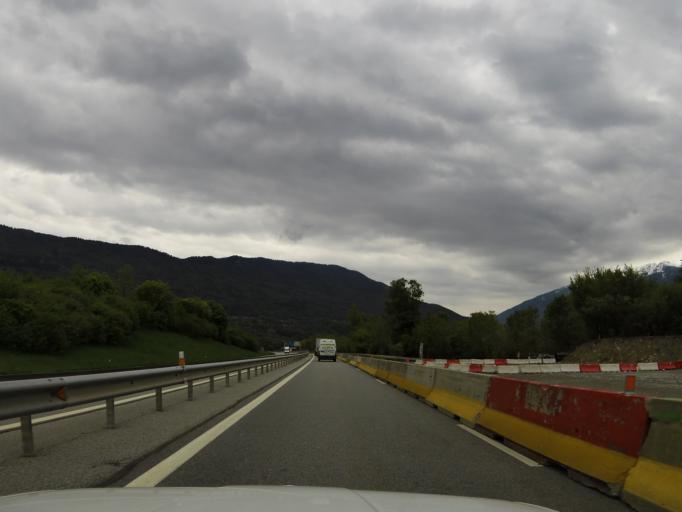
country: FR
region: Rhone-Alpes
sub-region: Departement de la Savoie
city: Saint-Remy-de-Maurienne
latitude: 45.4654
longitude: 6.2904
